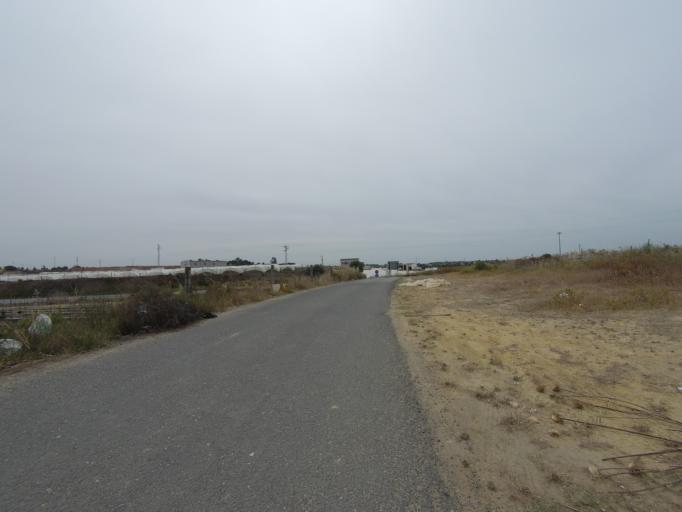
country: ES
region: Andalusia
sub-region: Provincia de Huelva
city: Palos de la Frontera
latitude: 37.2418
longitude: -6.8815
